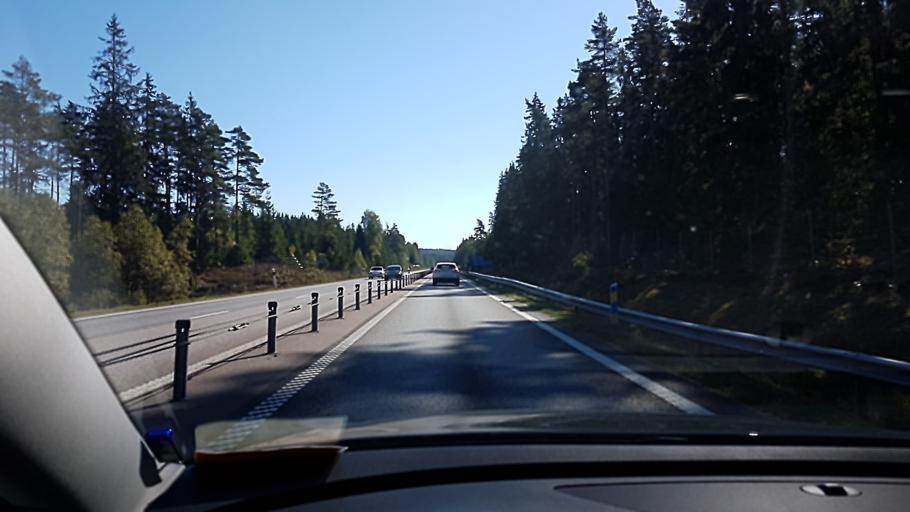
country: SE
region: Kronoberg
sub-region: Lessebo Kommun
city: Hovmantorp
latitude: 56.8681
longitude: 15.0122
